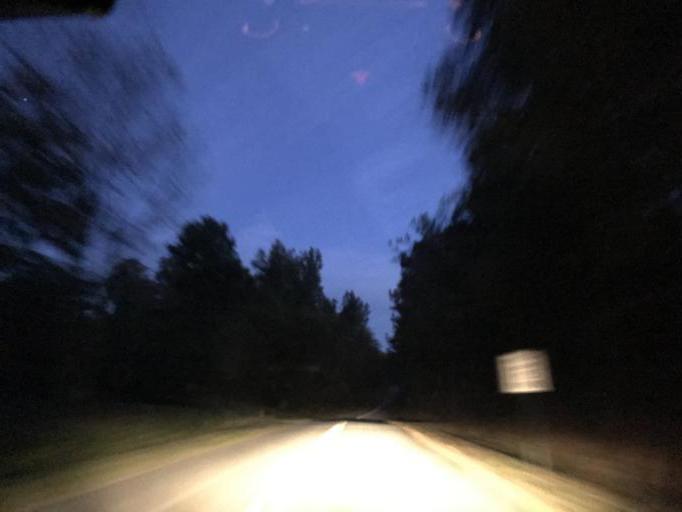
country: US
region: Georgia
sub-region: Jones County
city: Gray
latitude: 32.9200
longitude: -83.5130
